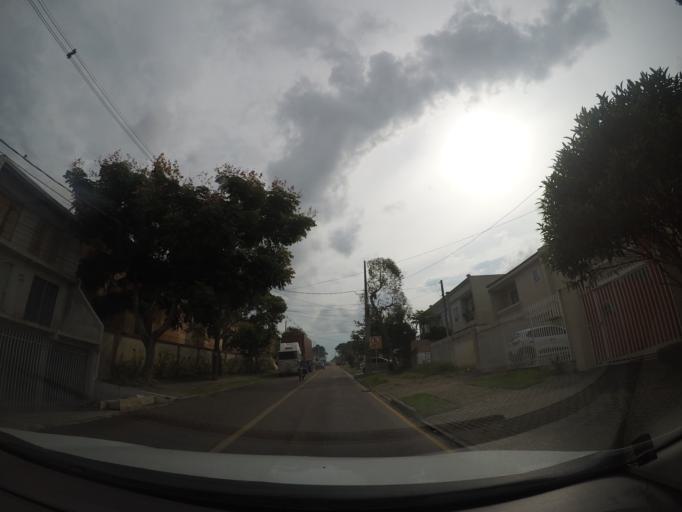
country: BR
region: Parana
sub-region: Sao Jose Dos Pinhais
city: Sao Jose dos Pinhais
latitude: -25.5213
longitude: -49.2503
